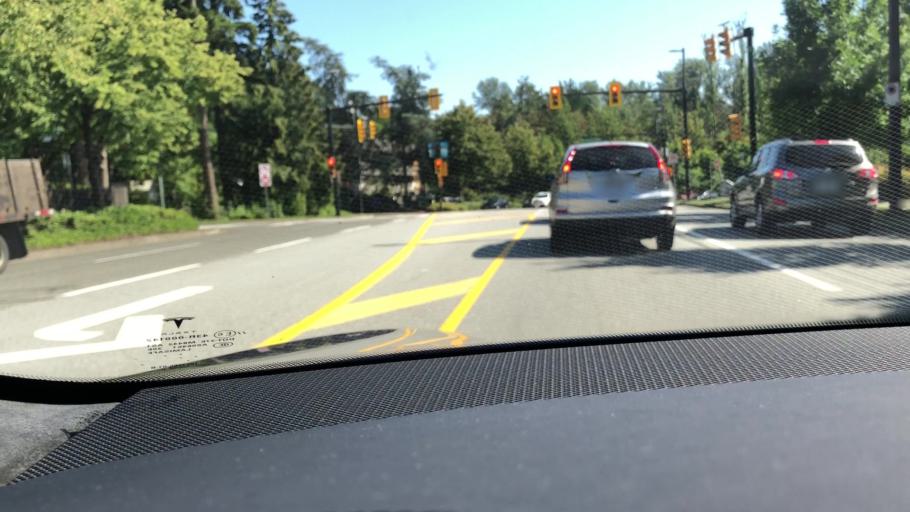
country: CA
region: British Columbia
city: Burnaby
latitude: 49.2437
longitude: -122.9755
